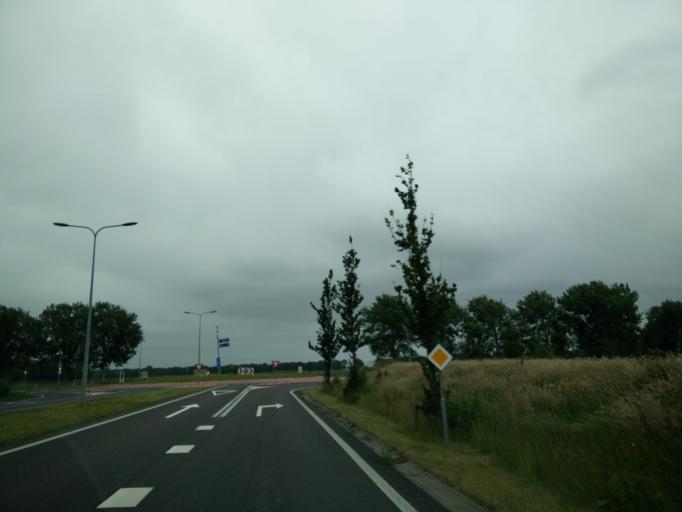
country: NL
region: Groningen
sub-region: Gemeente Groningen
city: Groningen
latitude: 53.1976
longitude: 6.5117
